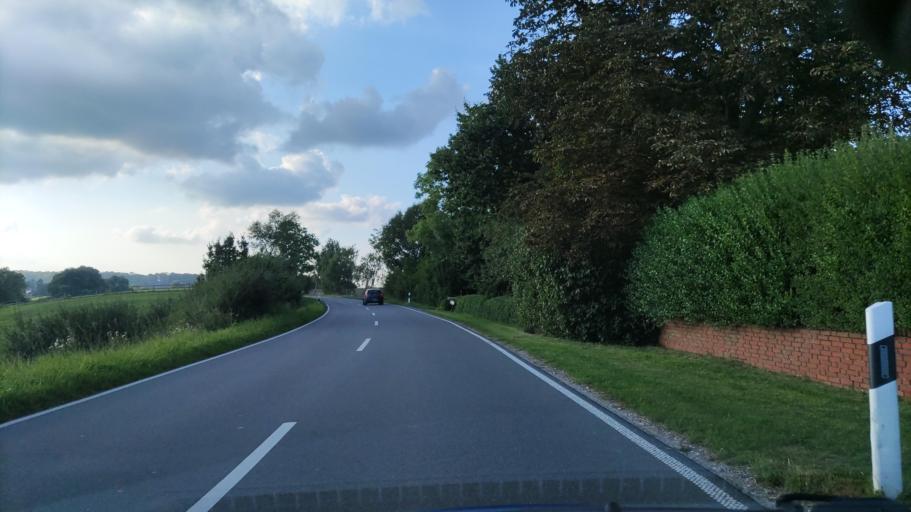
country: DE
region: Schleswig-Holstein
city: Glasau
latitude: 54.0364
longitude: 10.5462
